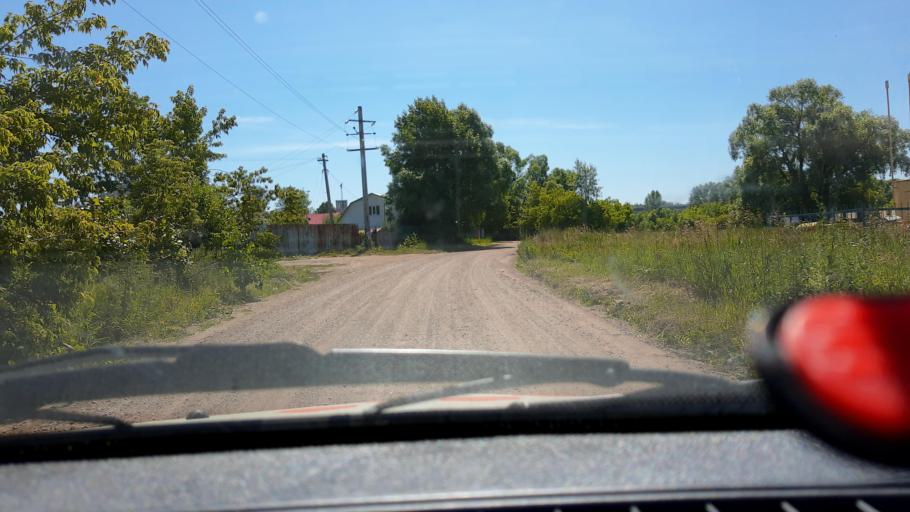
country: RU
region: Bashkortostan
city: Mikhaylovka
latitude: 54.7084
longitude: 55.8666
